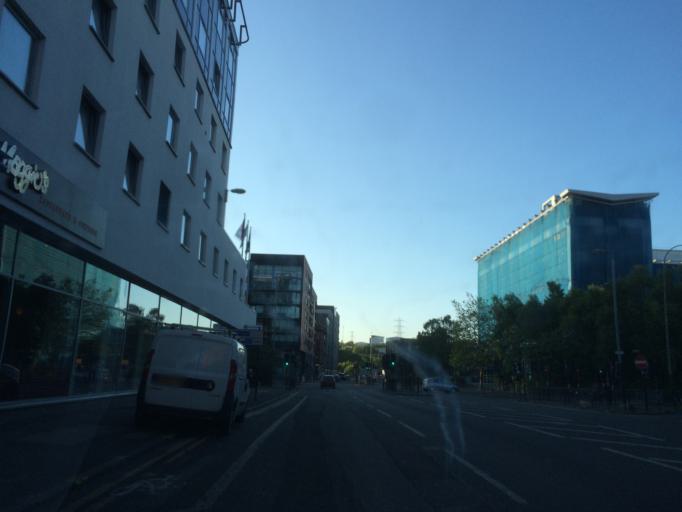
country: GB
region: Scotland
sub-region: Glasgow City
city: Glasgow
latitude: 55.8656
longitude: -4.2537
